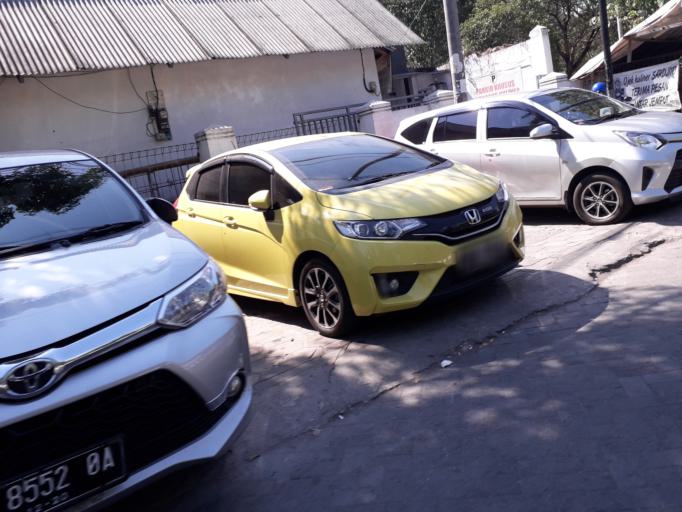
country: ID
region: Daerah Istimewa Yogyakarta
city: Yogyakarta
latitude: -7.7675
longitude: 110.3744
